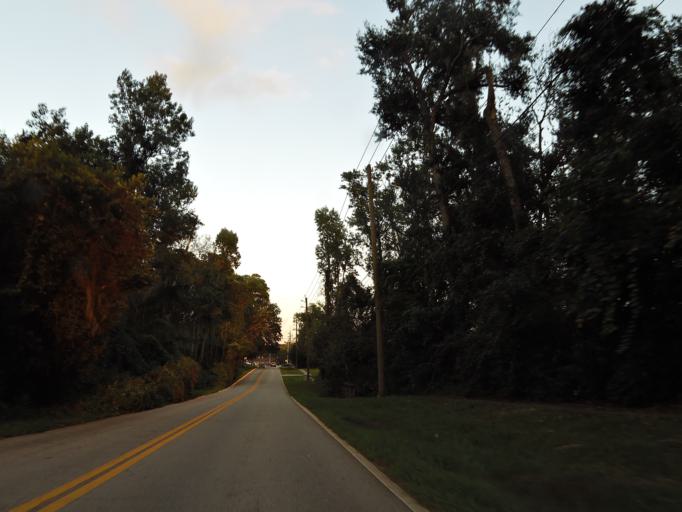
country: US
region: Florida
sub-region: Saint Johns County
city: Fruit Cove
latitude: 30.1903
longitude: -81.6301
